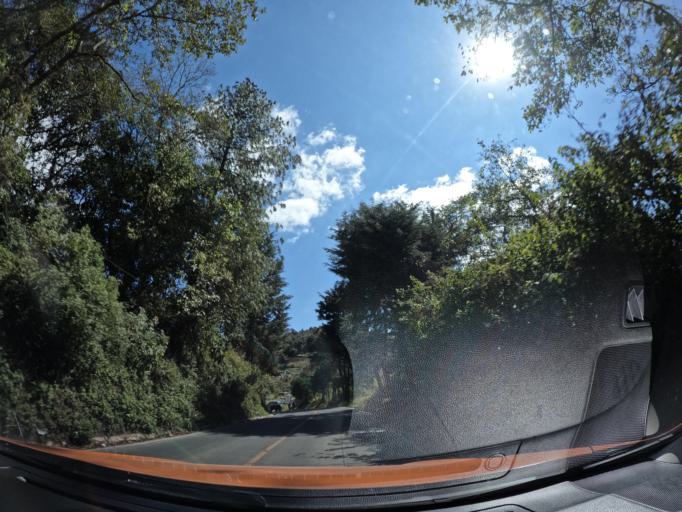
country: GT
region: Chimaltenango
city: Patzun
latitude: 14.6499
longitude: -91.0464
